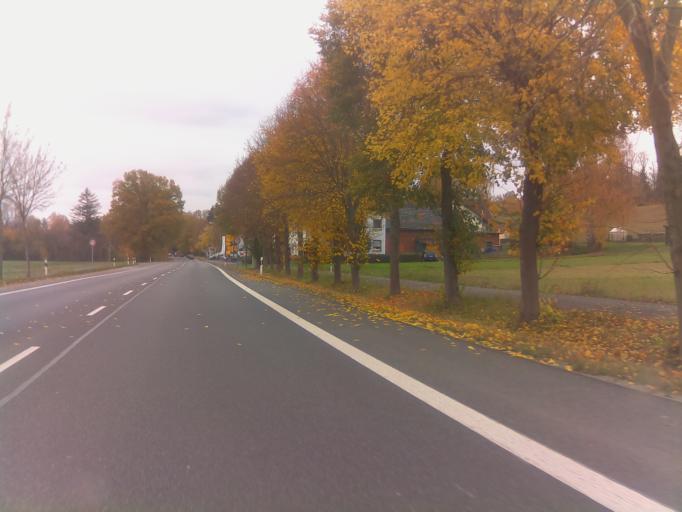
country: DE
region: Hesse
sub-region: Regierungsbezirk Kassel
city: Fulda
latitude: 50.5631
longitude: 9.6419
